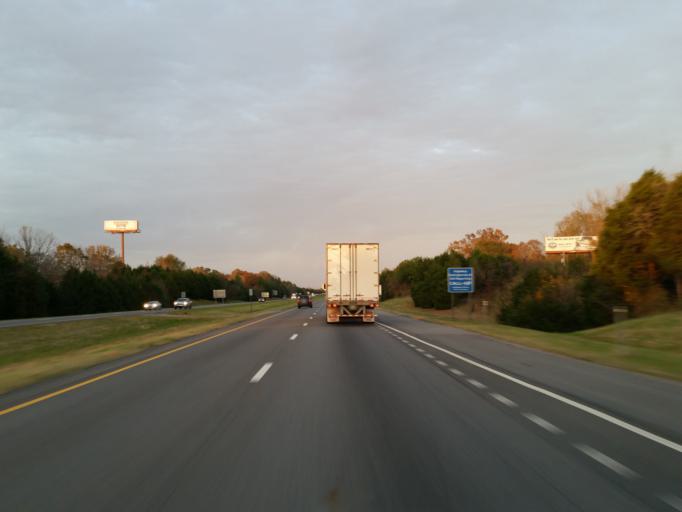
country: US
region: Alabama
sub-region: Sumter County
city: Livingston
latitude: 32.6311
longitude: -88.2050
